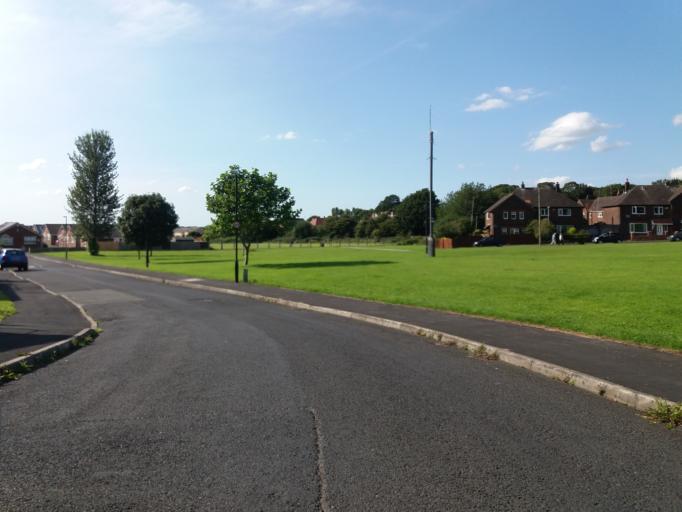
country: GB
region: England
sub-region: Lancashire
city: Coppull
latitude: 53.6427
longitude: -2.6446
